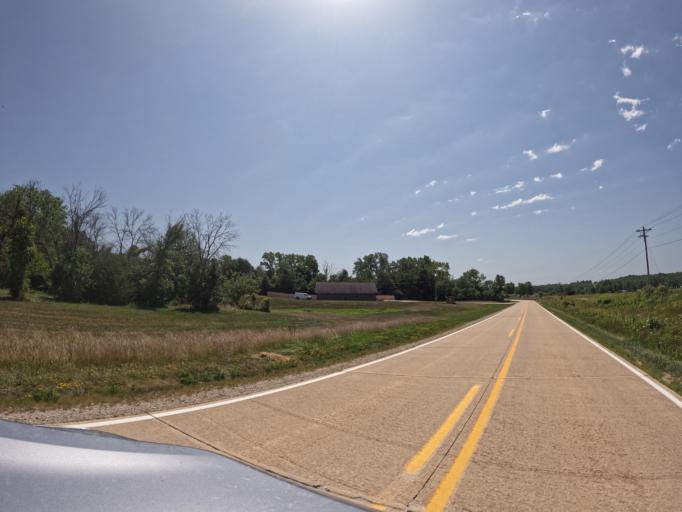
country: US
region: Iowa
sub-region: Henry County
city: Mount Pleasant
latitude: 40.9050
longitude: -91.5543
